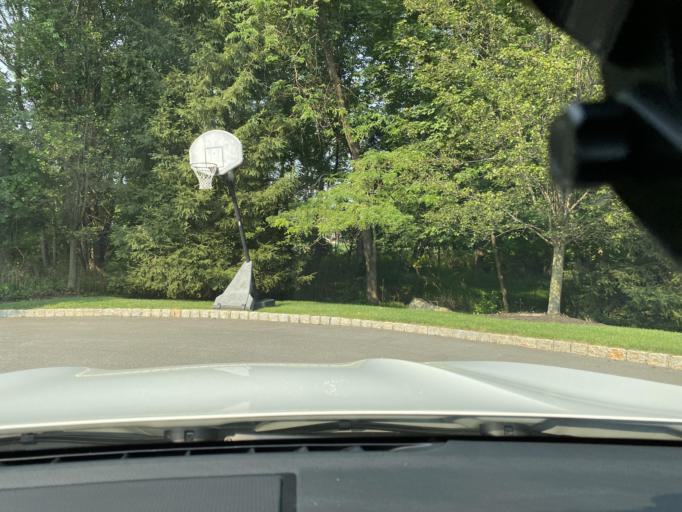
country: US
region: New York
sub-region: Rockland County
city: Airmont
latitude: 41.0873
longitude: -74.1233
